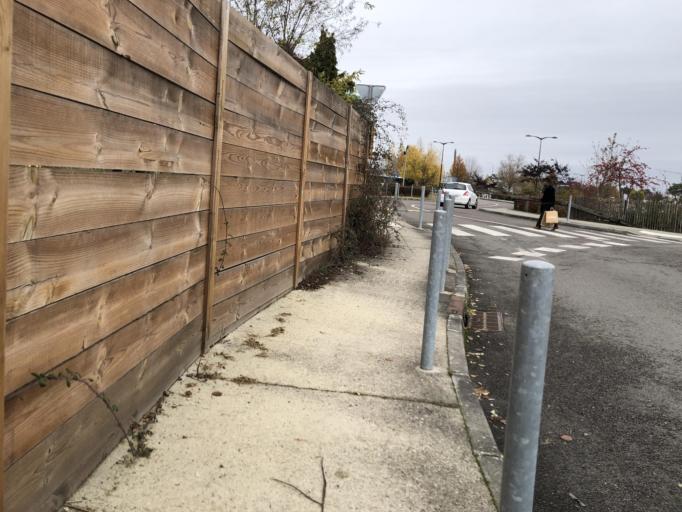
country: FR
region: Aquitaine
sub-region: Departement de la Gironde
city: Merignac
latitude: 44.8291
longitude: -0.6602
